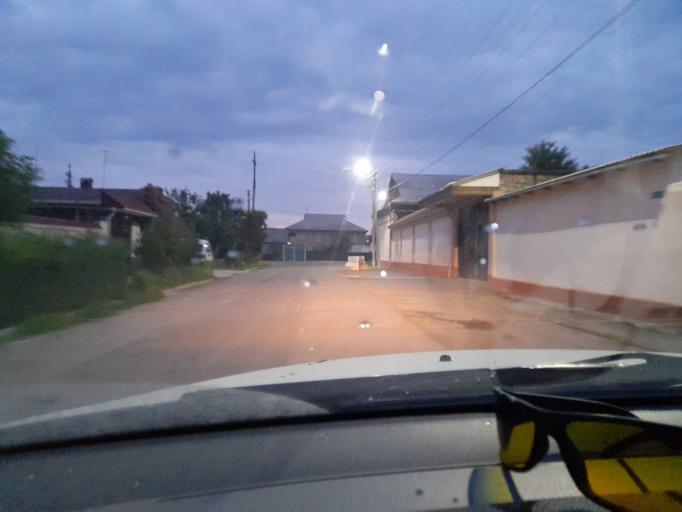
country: UZ
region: Sirdaryo
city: Guliston
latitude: 40.5040
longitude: 68.7804
